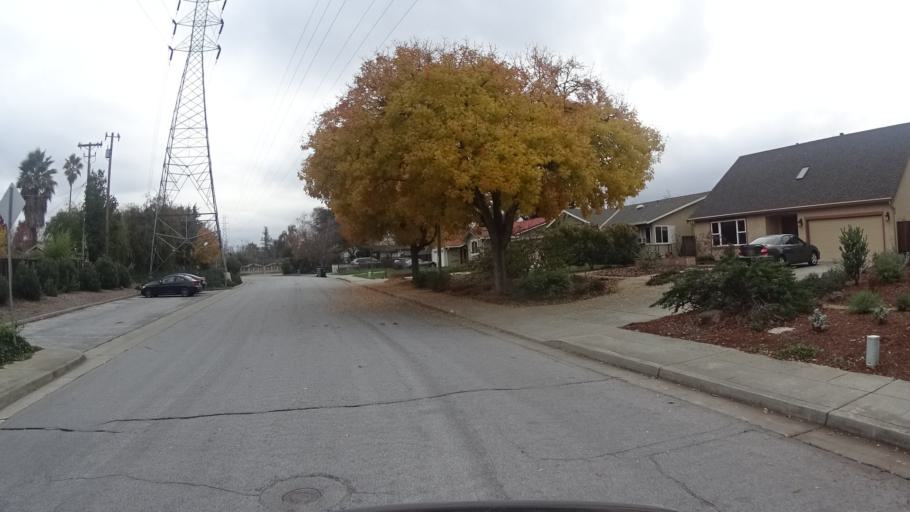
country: US
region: California
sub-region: Santa Clara County
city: Sunnyvale
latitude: 37.3595
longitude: -122.0616
